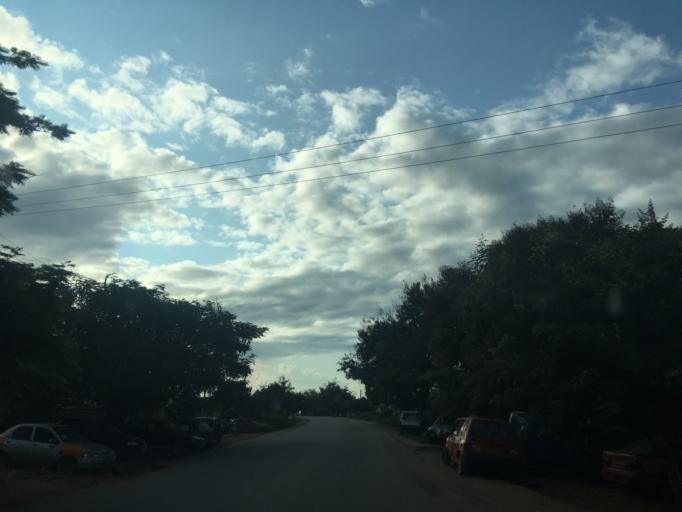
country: GH
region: Western
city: Bibiani
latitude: 6.3376
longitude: -2.2710
